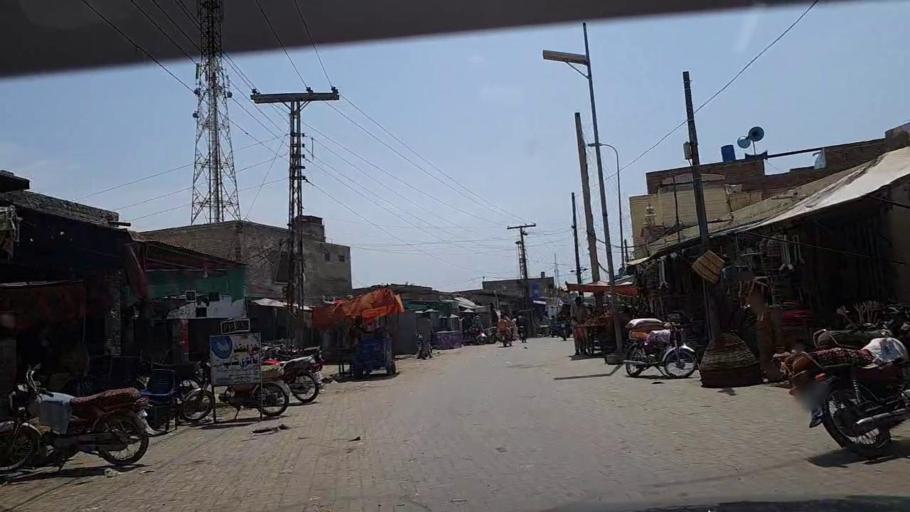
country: PK
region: Sindh
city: Khanpur
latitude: 27.8448
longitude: 69.4157
